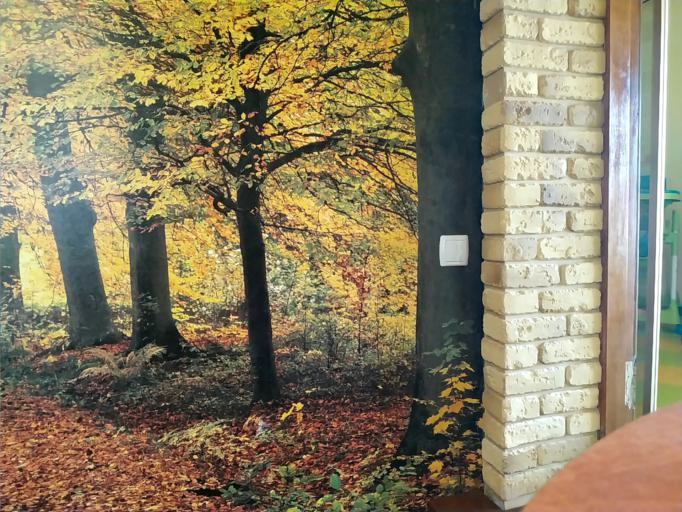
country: RU
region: Tverskaya
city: Maksatikha
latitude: 57.5671
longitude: 35.9445
